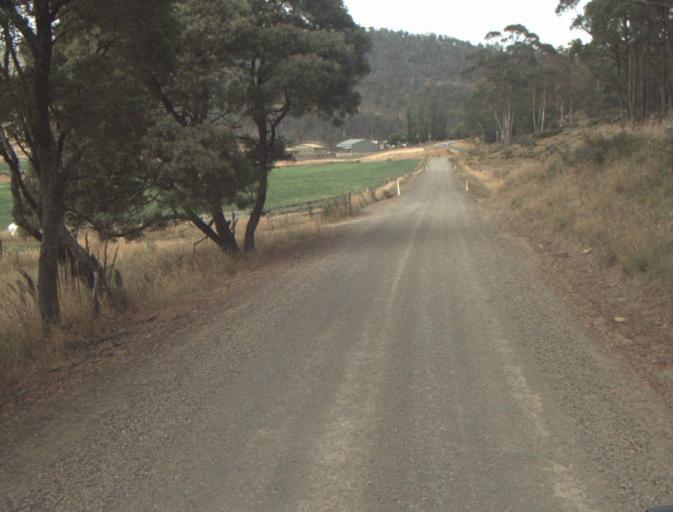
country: AU
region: Tasmania
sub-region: Northern Midlands
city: Evandale
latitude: -41.4824
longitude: 147.4419
